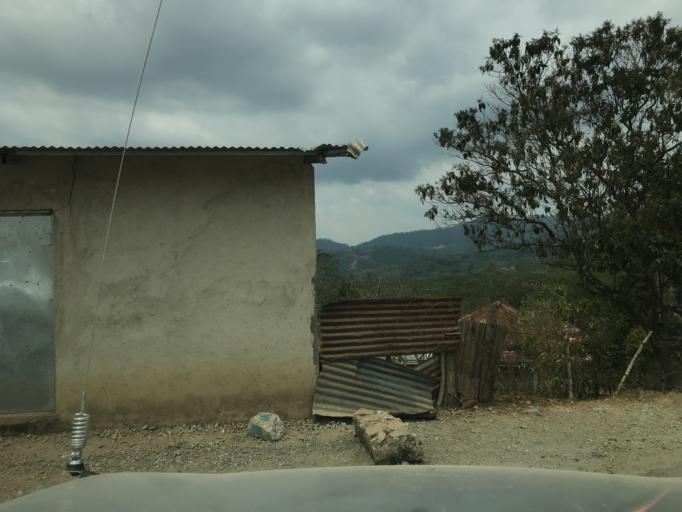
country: TL
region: Ermera
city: Gleno
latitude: -8.8355
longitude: 125.4276
